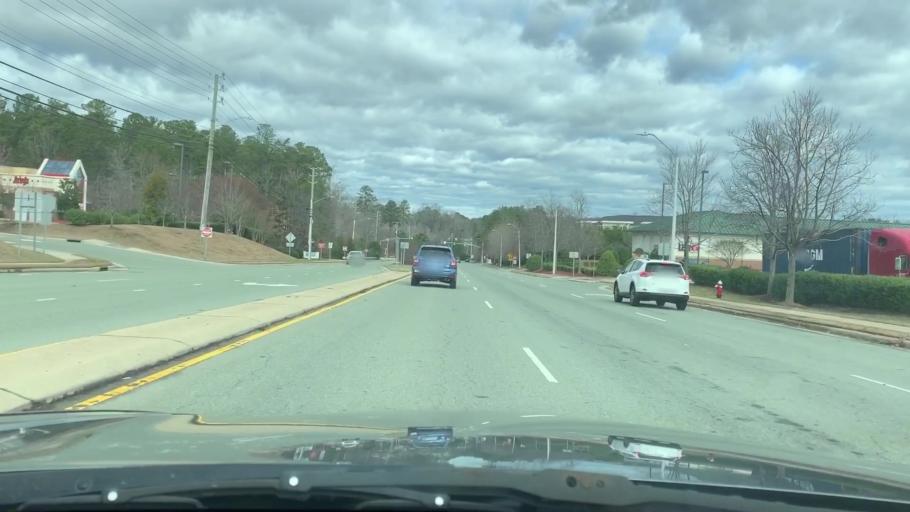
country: US
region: North Carolina
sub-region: Wake County
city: Cary
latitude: 35.8036
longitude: -78.7829
